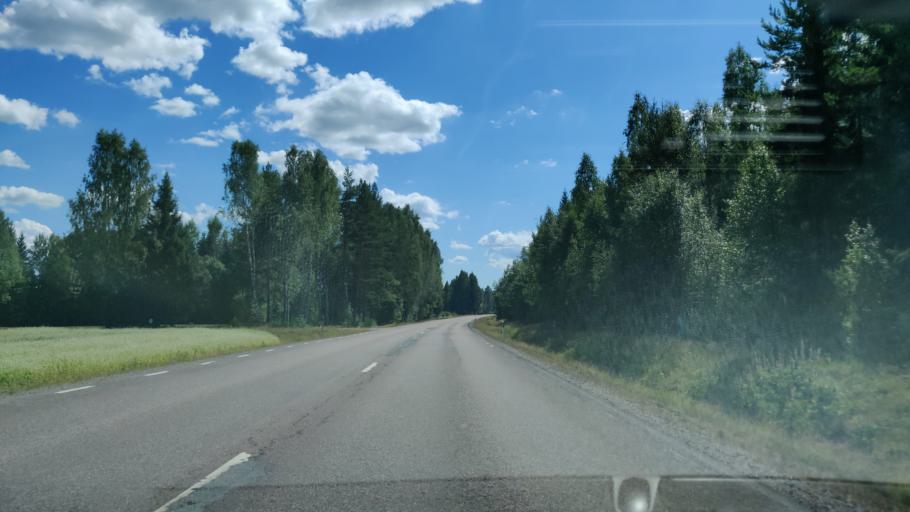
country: SE
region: Vaermland
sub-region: Hagfors Kommun
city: Ekshaerad
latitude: 60.1948
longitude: 13.4970
